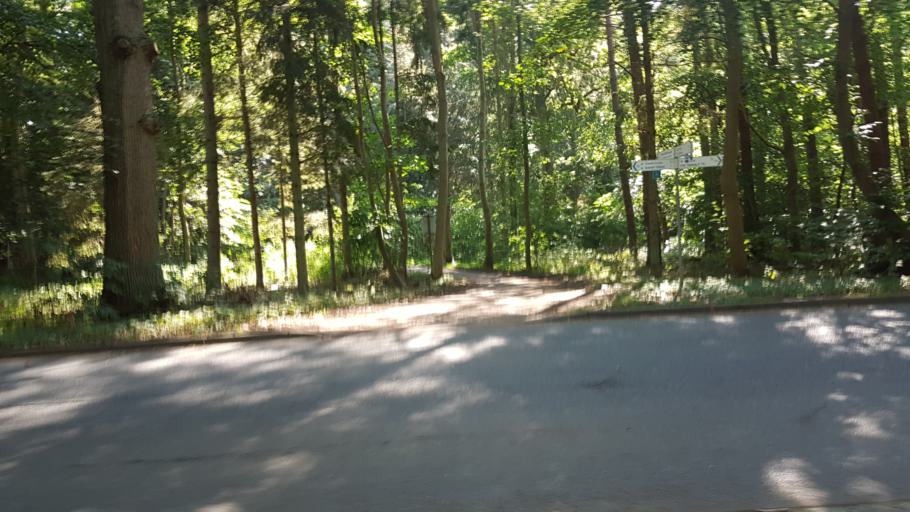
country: DE
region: Mecklenburg-Vorpommern
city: Ostseebad Gohren
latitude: 54.3444
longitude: 13.7236
